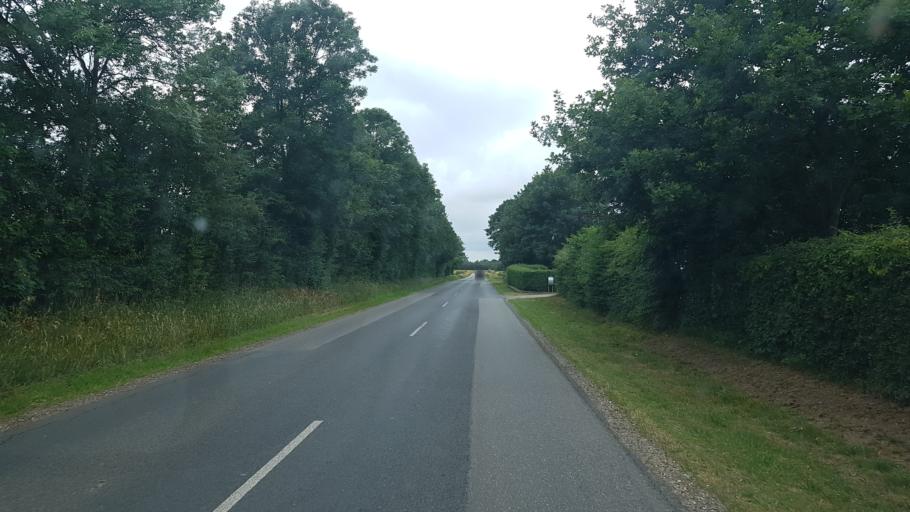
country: DK
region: South Denmark
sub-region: Kolding Kommune
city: Vamdrup
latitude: 55.4323
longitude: 9.2265
